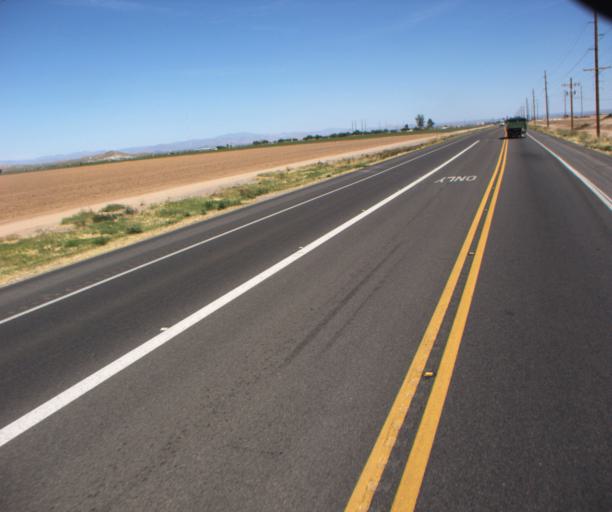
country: US
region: Arizona
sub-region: Pinal County
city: Blackwater
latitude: 33.0024
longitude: -111.5583
